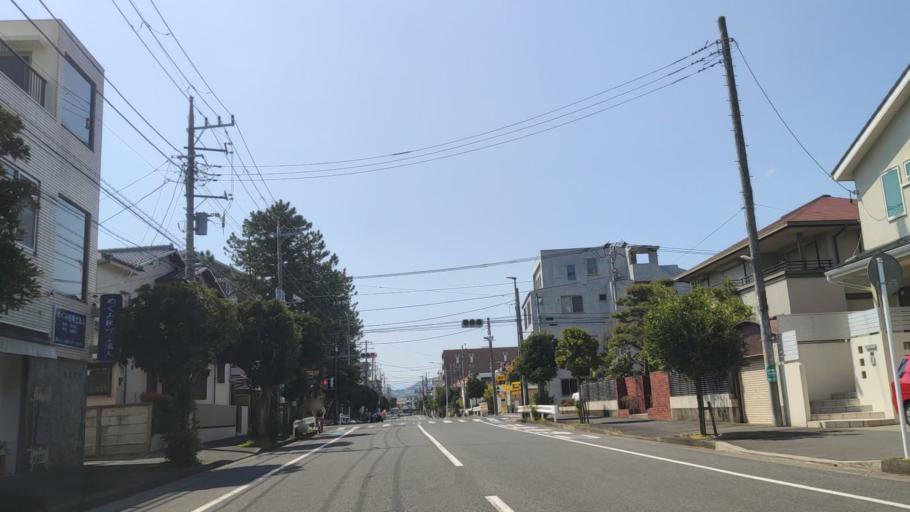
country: JP
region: Kanagawa
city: Hiratsuka
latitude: 35.3242
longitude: 139.3502
